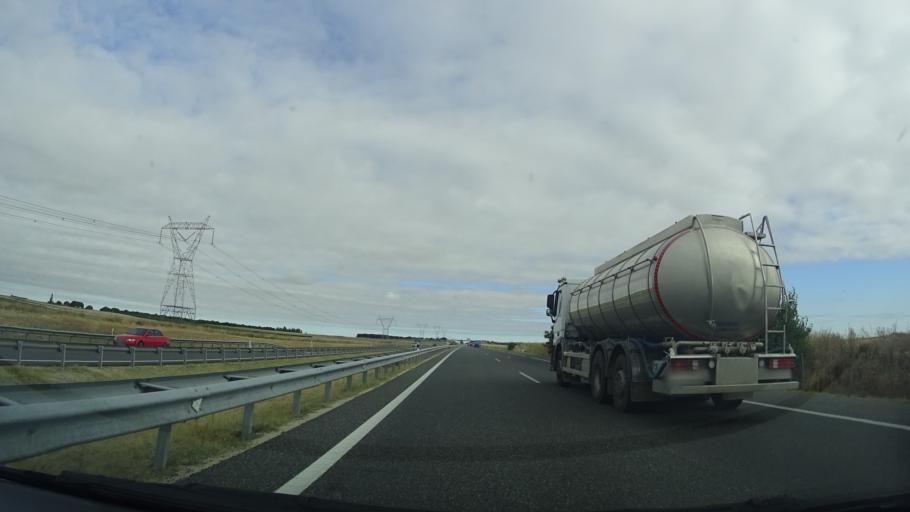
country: ES
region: Castille and Leon
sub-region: Provincia de Avila
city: Palacios de Goda
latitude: 41.1389
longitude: -4.7809
